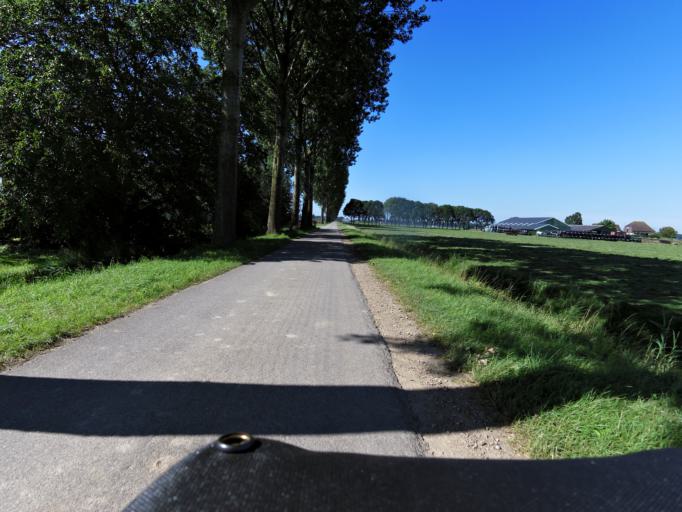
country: NL
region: South Holland
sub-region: Gemeente Dordrecht
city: Dordrecht
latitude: 51.7588
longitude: 4.7219
